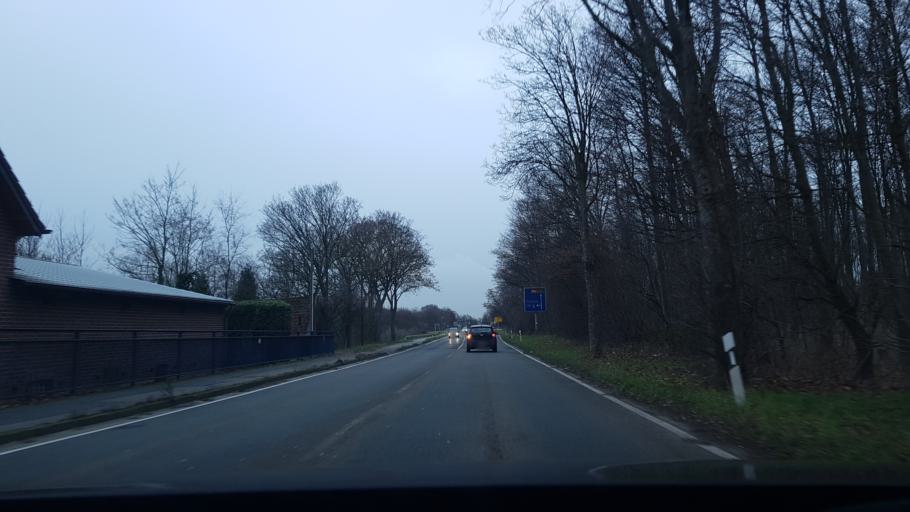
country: DE
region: North Rhine-Westphalia
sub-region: Regierungsbezirk Dusseldorf
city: Moers
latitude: 51.4332
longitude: 6.6468
